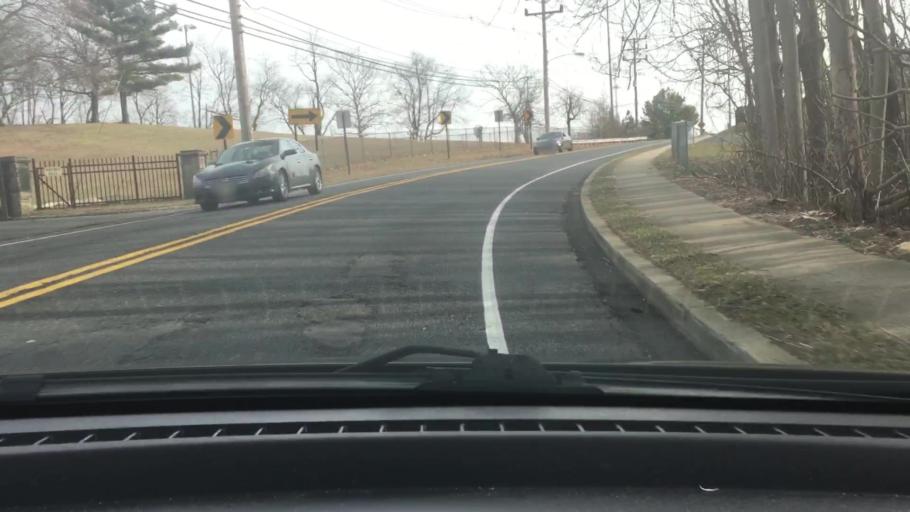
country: US
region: New Jersey
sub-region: Monmouth County
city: Shark River Hills
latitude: 40.2197
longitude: -74.0492
